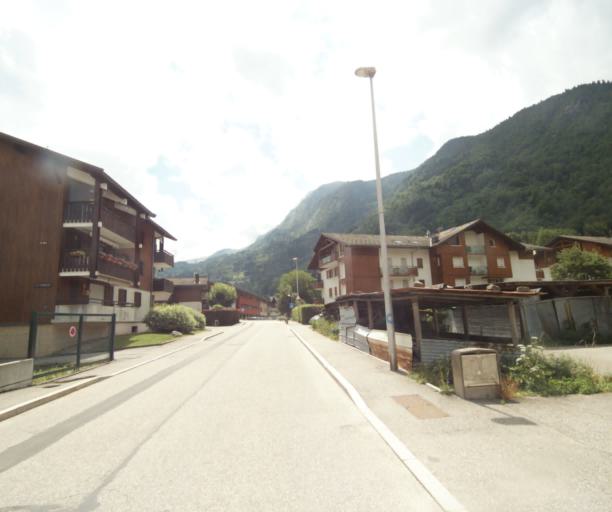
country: FR
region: Rhone-Alpes
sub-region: Departement de la Haute-Savoie
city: Thones
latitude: 45.8792
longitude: 6.3231
